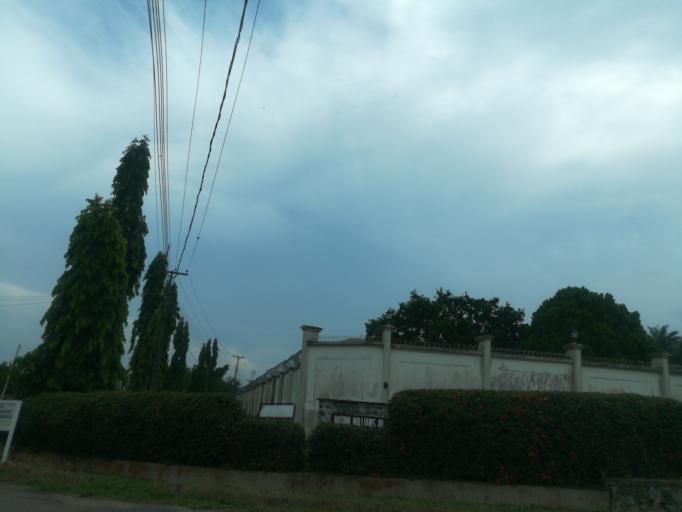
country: NG
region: Oyo
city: Ibadan
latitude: 7.4209
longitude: 3.9065
